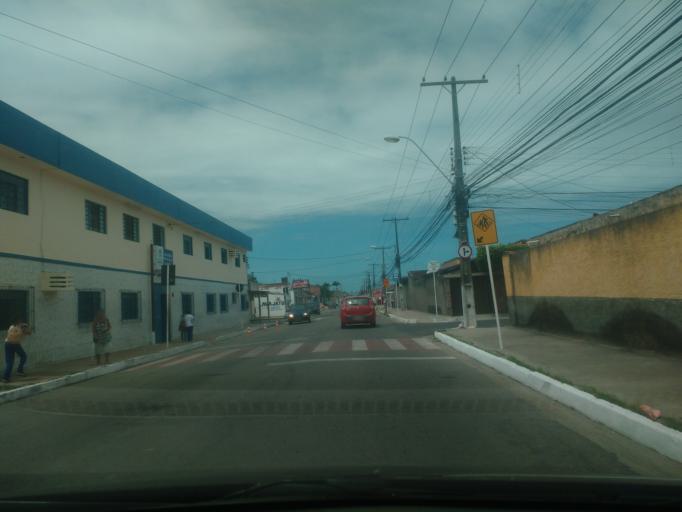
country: BR
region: Alagoas
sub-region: Satuba
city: Satuba
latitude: -9.5526
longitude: -35.7629
